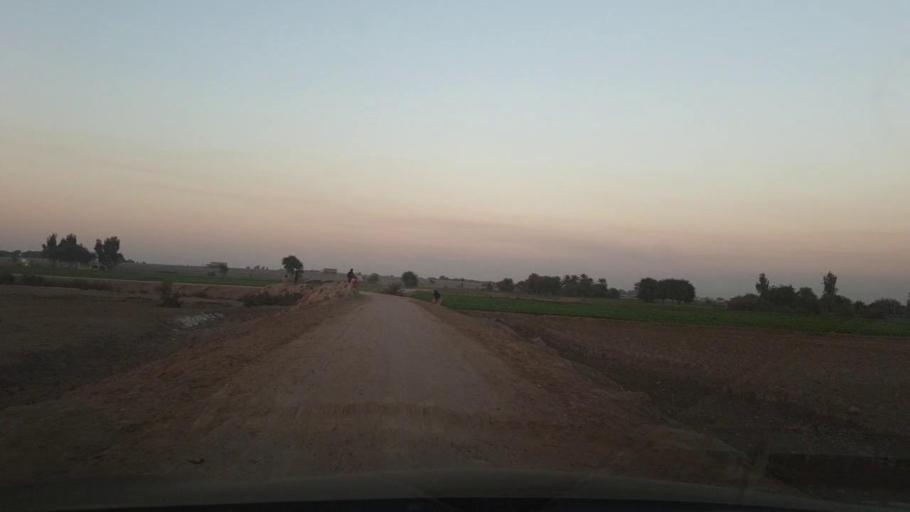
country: PK
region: Sindh
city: Ubauro
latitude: 28.1761
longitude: 69.6345
